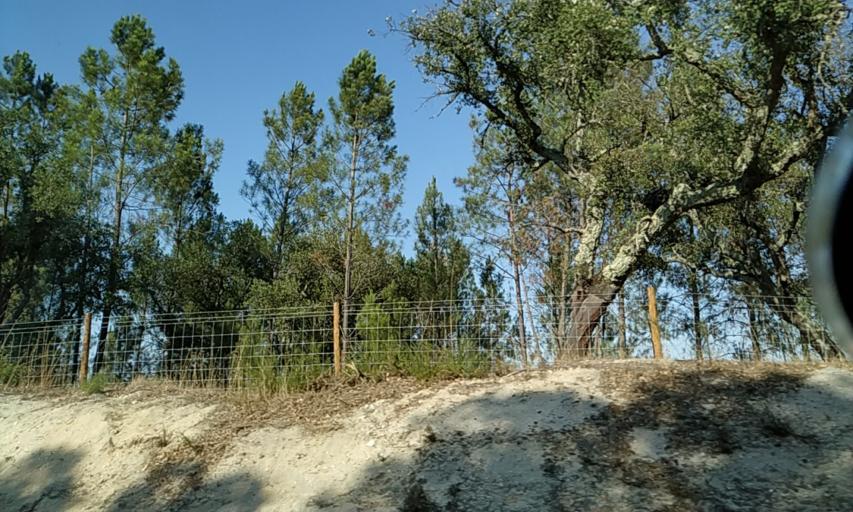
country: PT
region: Santarem
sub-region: Coruche
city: Coruche
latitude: 38.9992
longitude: -8.5568
